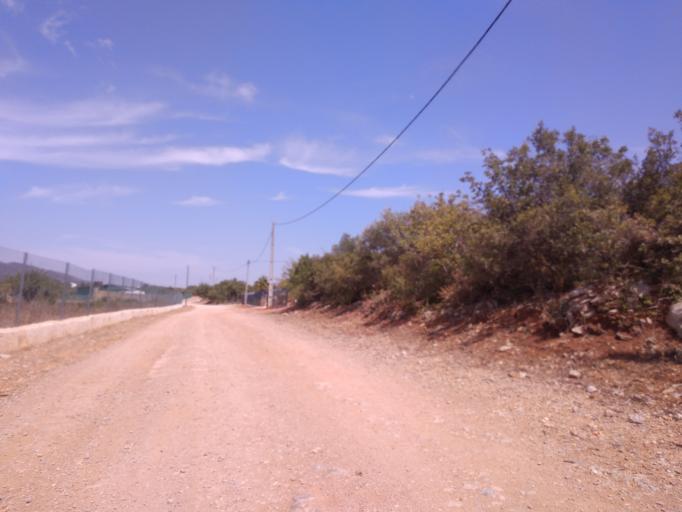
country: PT
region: Faro
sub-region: Faro
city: Santa Barbara de Nexe
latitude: 37.0922
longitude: -7.9724
